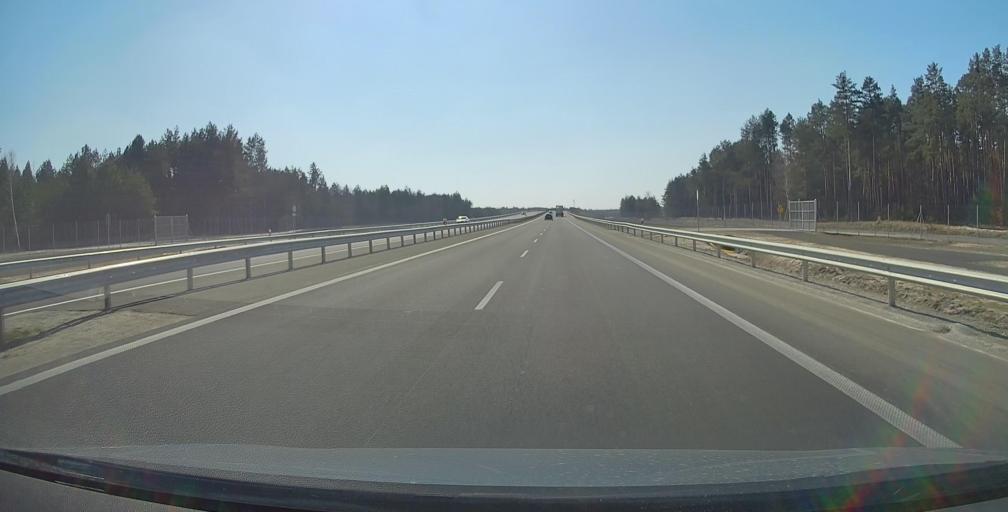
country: PL
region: Subcarpathian Voivodeship
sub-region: Powiat nizanski
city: Konczyce
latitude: 50.4446
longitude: 22.1403
